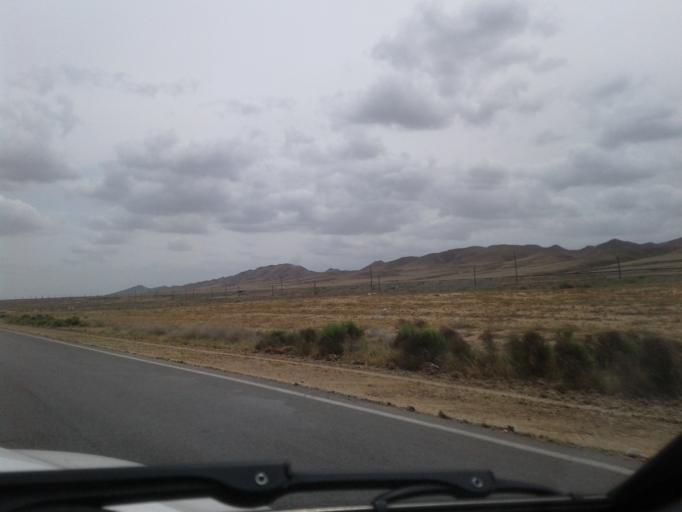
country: IR
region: Razavi Khorasan
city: Dargaz
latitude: 37.6235
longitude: 59.1694
